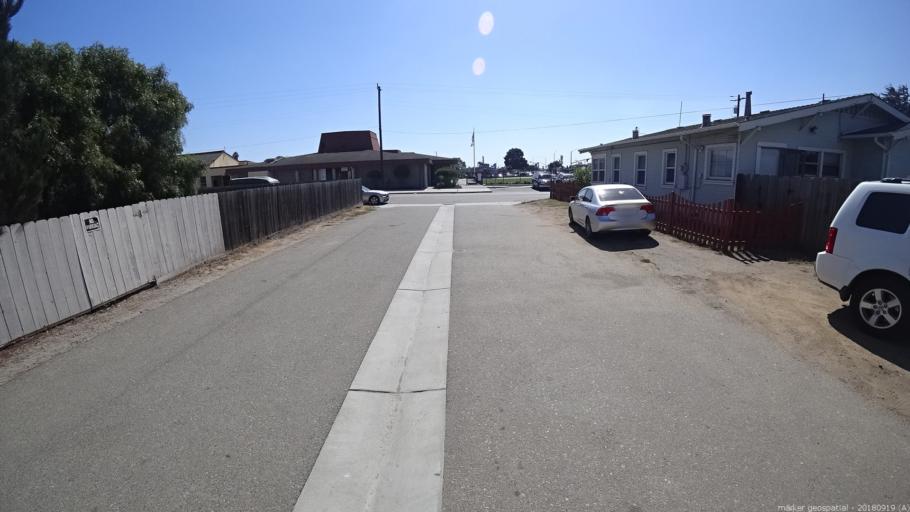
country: US
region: California
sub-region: Monterey County
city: Castroville
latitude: 36.7638
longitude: -121.7545
